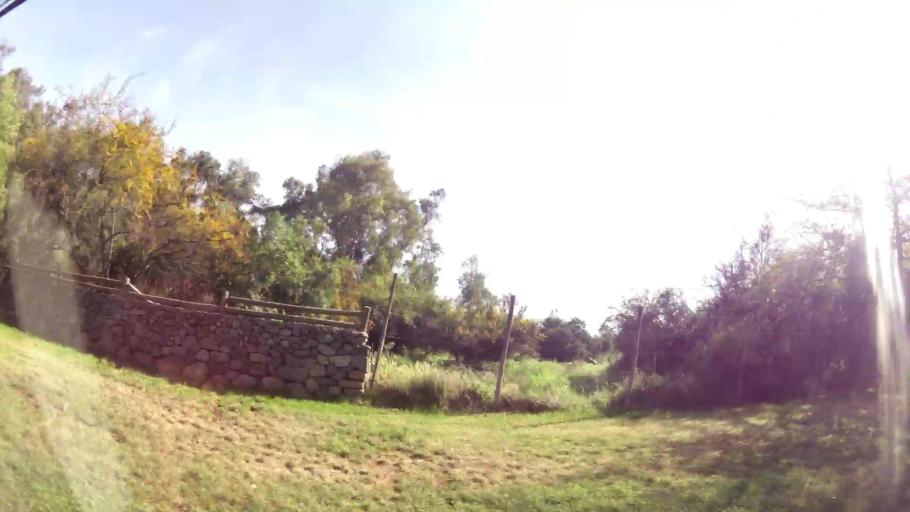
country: CL
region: Santiago Metropolitan
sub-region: Provincia de Santiago
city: Villa Presidente Frei, Nunoa, Santiago, Chile
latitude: -33.5012
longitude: -70.5428
